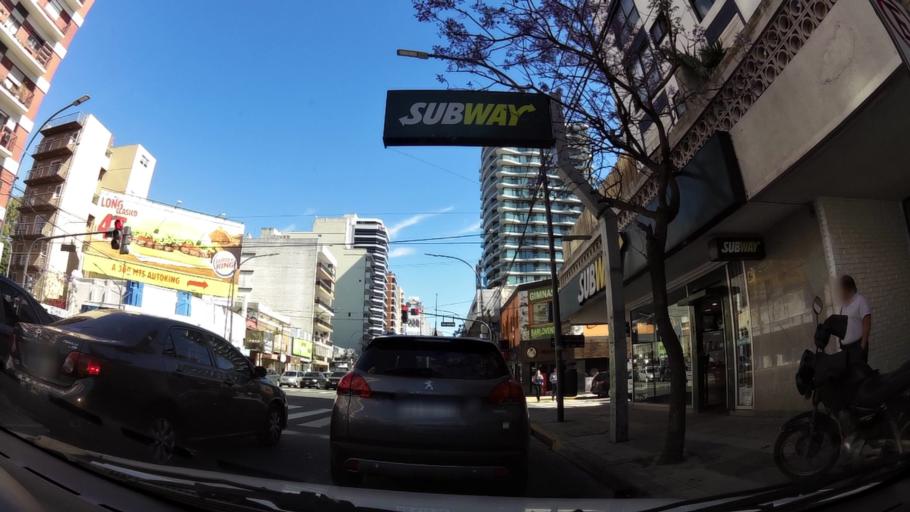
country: AR
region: Buenos Aires
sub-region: Partido de Vicente Lopez
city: Olivos
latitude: -34.5197
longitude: -58.4745
